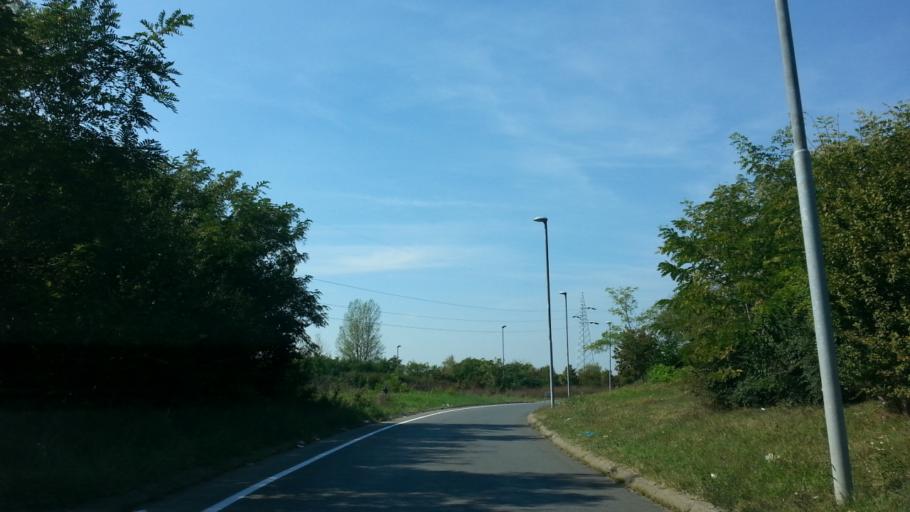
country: RS
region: Central Serbia
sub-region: Belgrade
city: Rakovica
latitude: 44.7416
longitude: 20.4143
